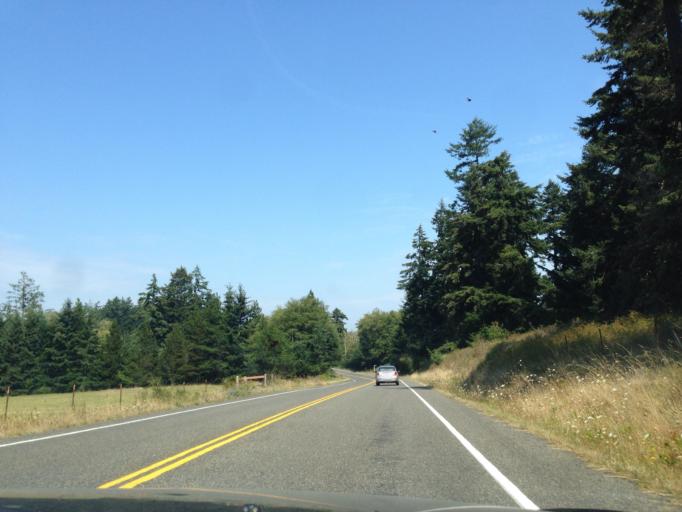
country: US
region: Washington
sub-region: San Juan County
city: Friday Harbor
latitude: 48.4951
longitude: -123.0326
